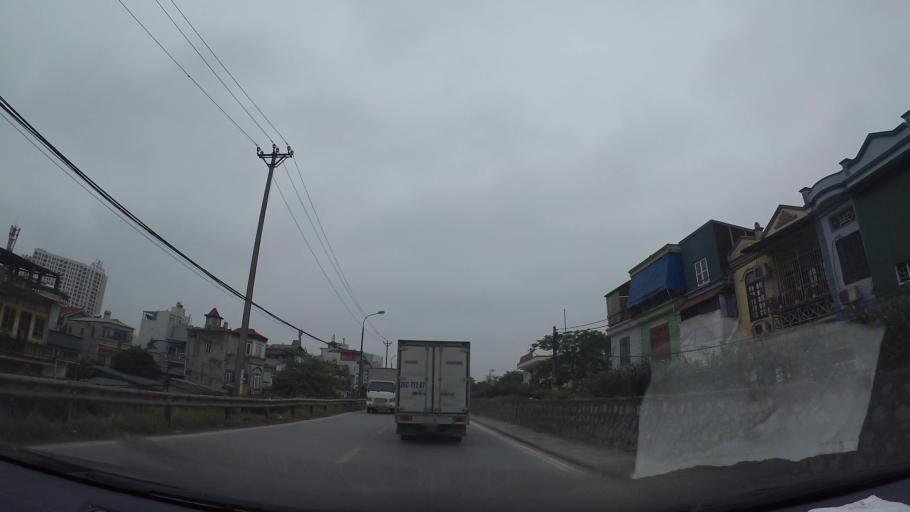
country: VN
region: Ha Noi
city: Hai BaTrung
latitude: 21.0010
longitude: 105.8835
